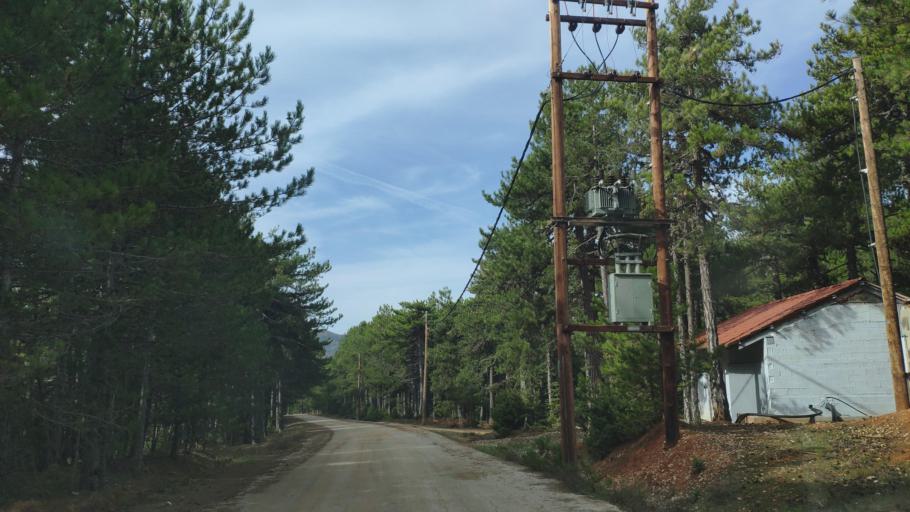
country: GR
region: West Greece
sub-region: Nomos Achaias
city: Aiyira
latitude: 38.0327
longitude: 22.3738
